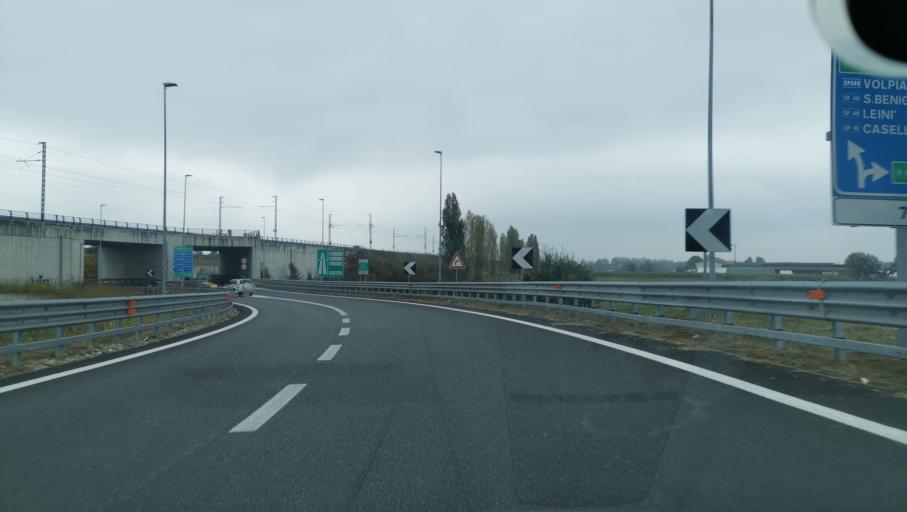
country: IT
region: Piedmont
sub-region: Provincia di Torino
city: Brandizzo
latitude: 45.1717
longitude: 7.8117
